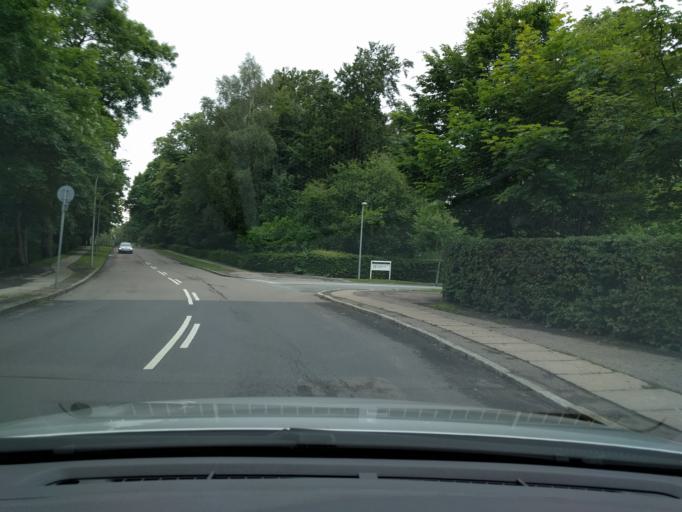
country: DK
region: Zealand
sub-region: Roskilde Kommune
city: Roskilde
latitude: 55.6494
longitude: 12.0692
